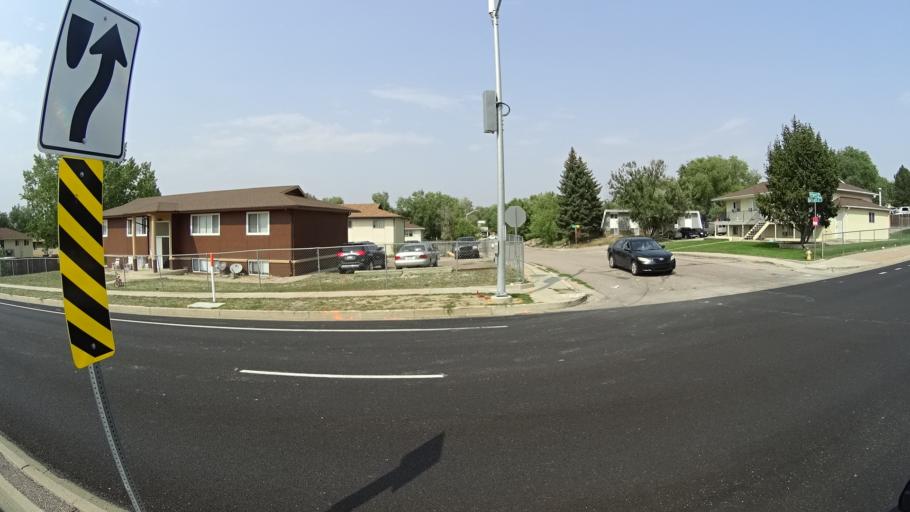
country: US
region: Colorado
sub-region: El Paso County
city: Cimarron Hills
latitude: 38.8253
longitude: -104.7466
